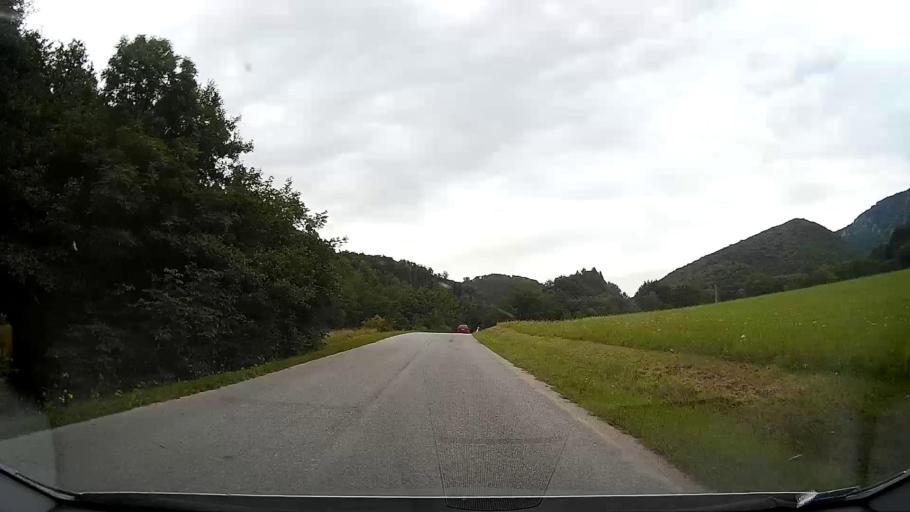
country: SK
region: Banskobystricky
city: Tisovec
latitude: 48.7143
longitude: 20.0023
